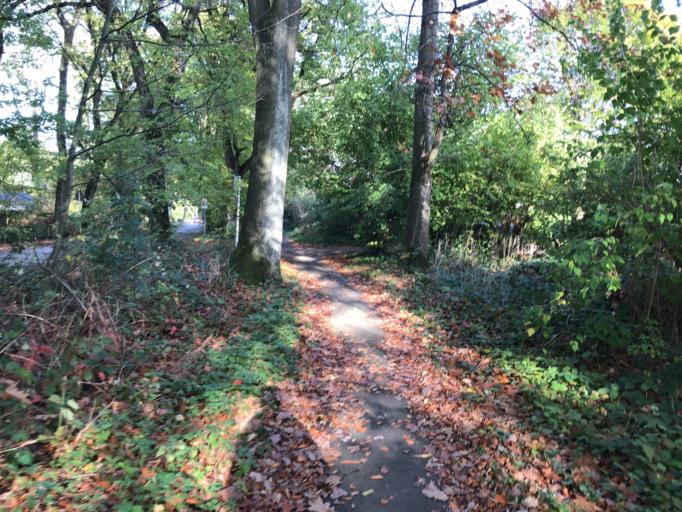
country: DE
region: North Rhine-Westphalia
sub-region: Regierungsbezirk Dusseldorf
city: Muelheim (Ruhr)
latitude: 51.4120
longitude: 6.8301
